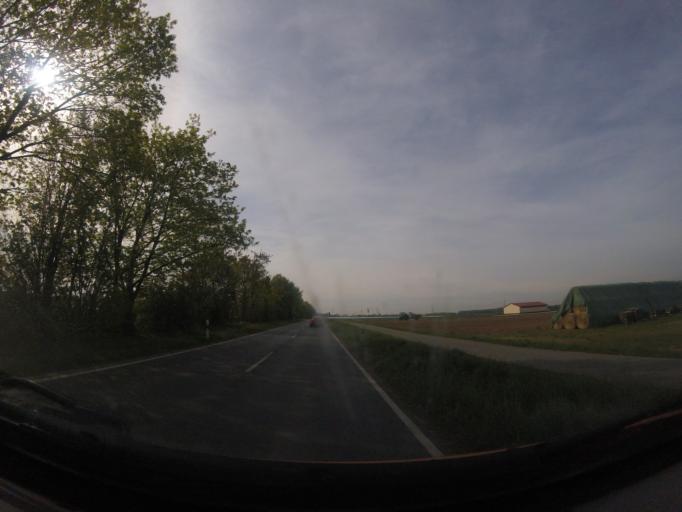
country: DE
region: Hesse
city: Griesheim
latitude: 49.8471
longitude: 8.5585
